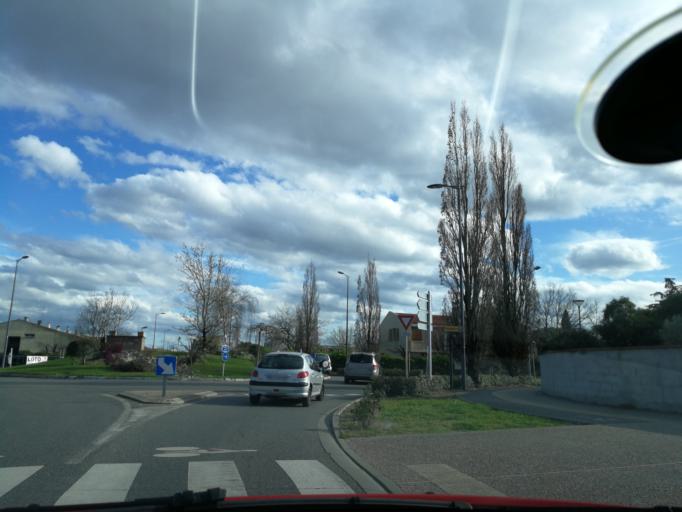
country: FR
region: Midi-Pyrenees
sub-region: Departement de la Haute-Garonne
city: Blagnac
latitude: 43.6429
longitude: 1.3868
